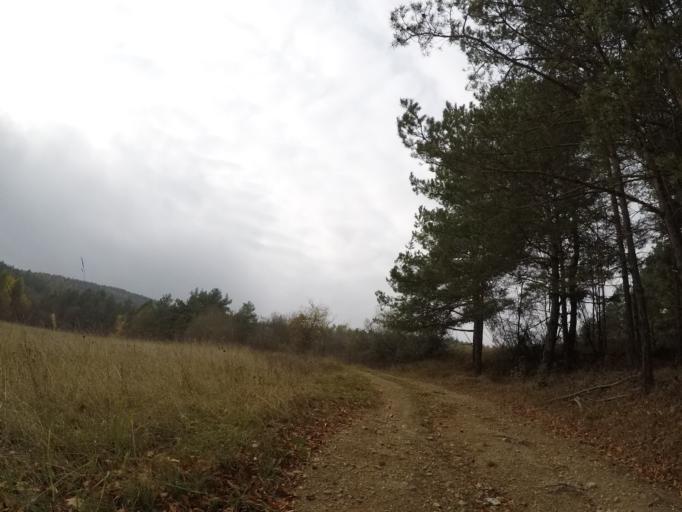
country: SK
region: Presovsky
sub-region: Okres Presov
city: Presov
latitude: 48.9035
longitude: 21.1726
